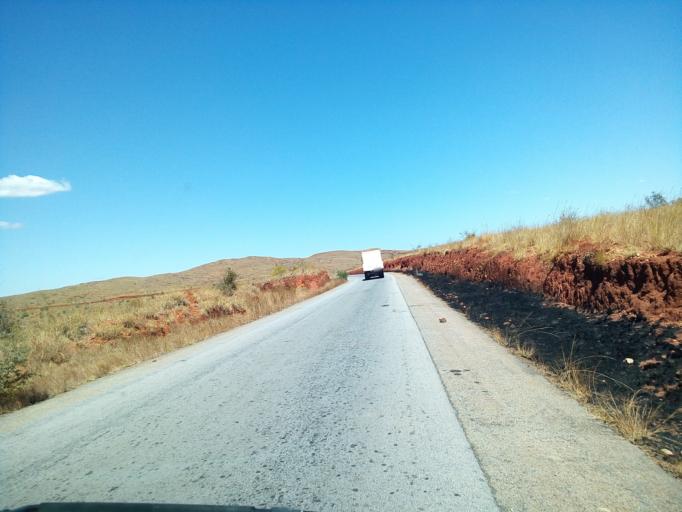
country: MG
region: Betsiboka
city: Maevatanana
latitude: -17.1364
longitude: 46.8126
